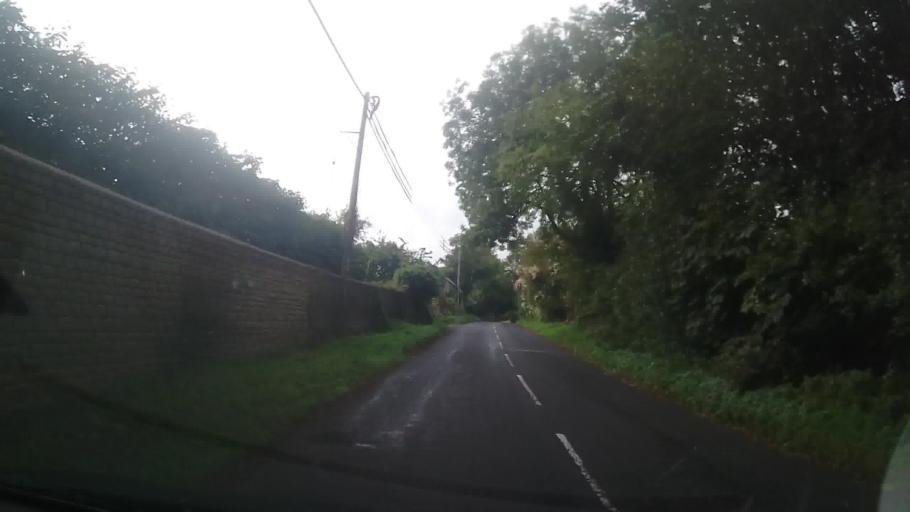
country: GB
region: England
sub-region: Oxfordshire
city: Chipping Norton
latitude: 51.9309
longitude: -1.5326
